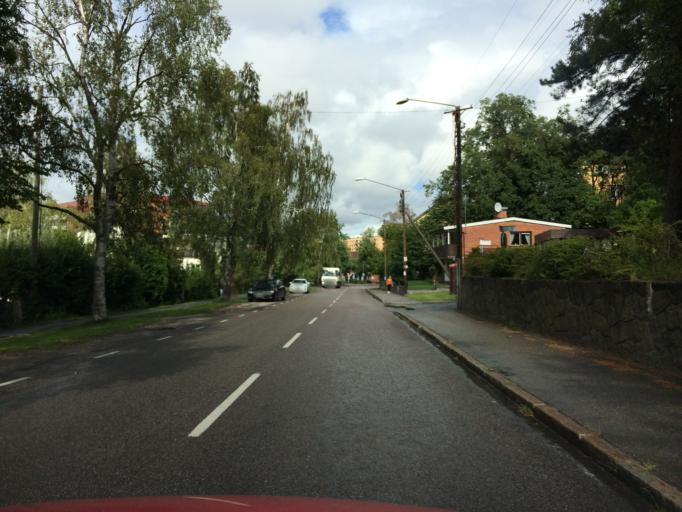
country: SE
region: Stockholm
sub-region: Stockholms Kommun
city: Bromma
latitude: 59.3026
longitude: 17.9731
